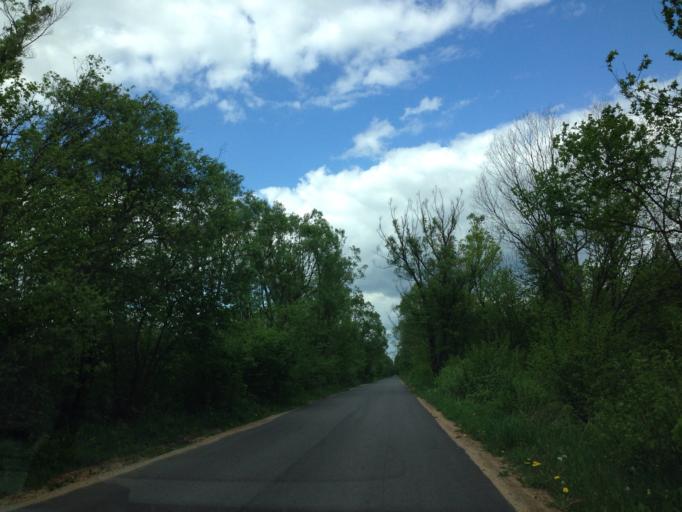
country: PL
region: Podlasie
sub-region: Powiat bialostocki
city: Tykocin
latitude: 53.3206
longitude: 22.6016
